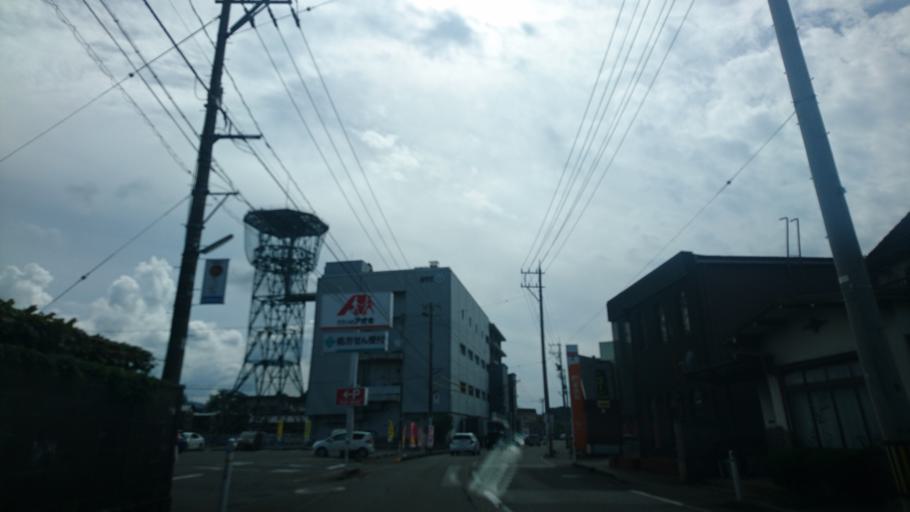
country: JP
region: Fukui
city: Maruoka
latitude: 36.3086
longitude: 136.3162
